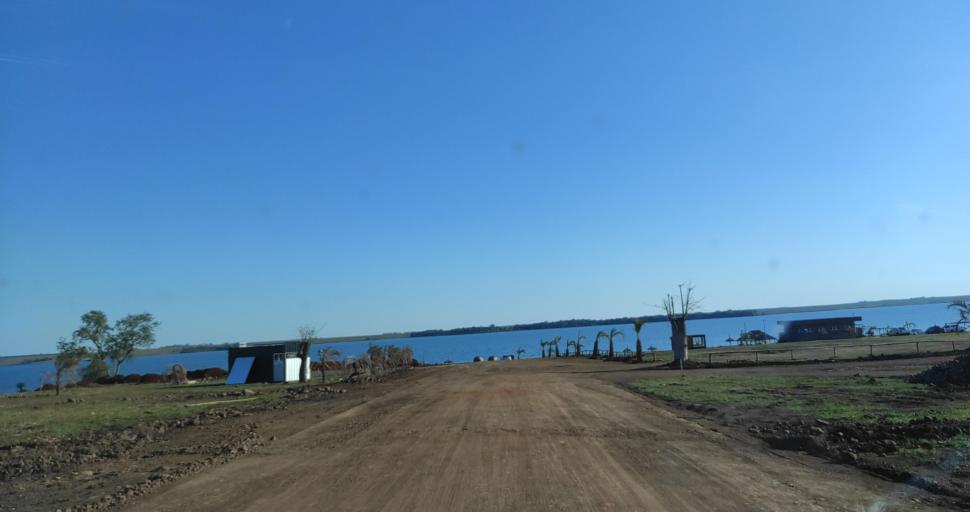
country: PY
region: Itapua
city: Carmen del Parana
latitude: -27.4111
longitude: -56.1825
